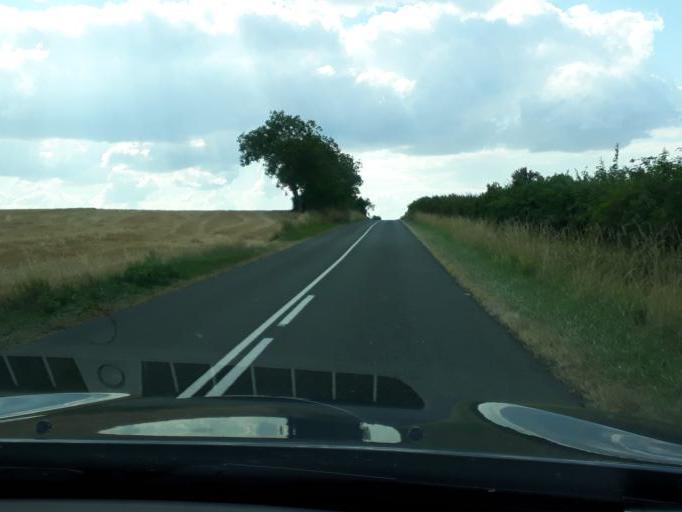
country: FR
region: Centre
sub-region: Departement du Cher
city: Baugy
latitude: 47.0909
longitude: 2.7055
